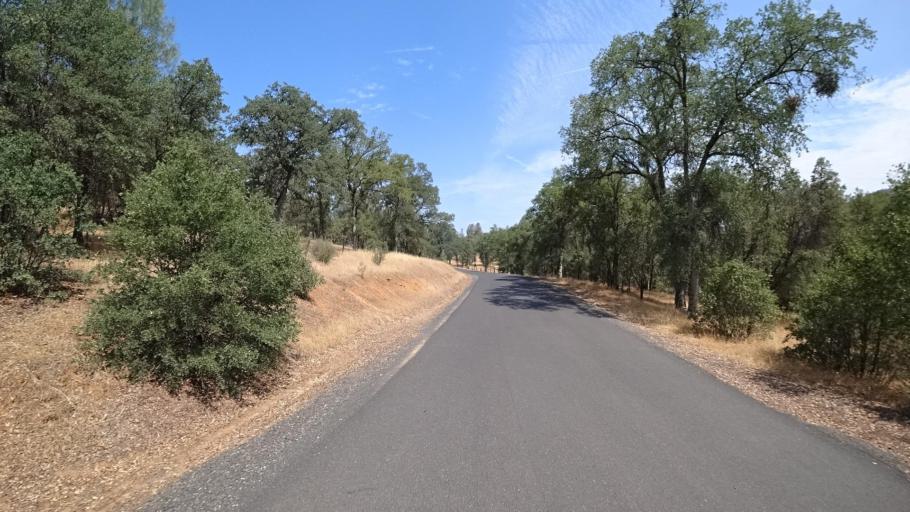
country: US
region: California
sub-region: Tuolumne County
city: Tuolumne City
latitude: 37.7142
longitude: -120.1821
